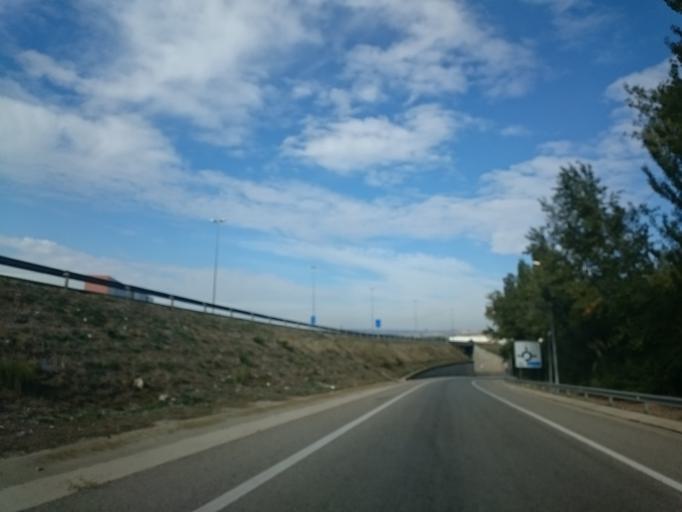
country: ES
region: Catalonia
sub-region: Provincia de Lleida
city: Alcoletge
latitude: 41.6170
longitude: 0.6667
